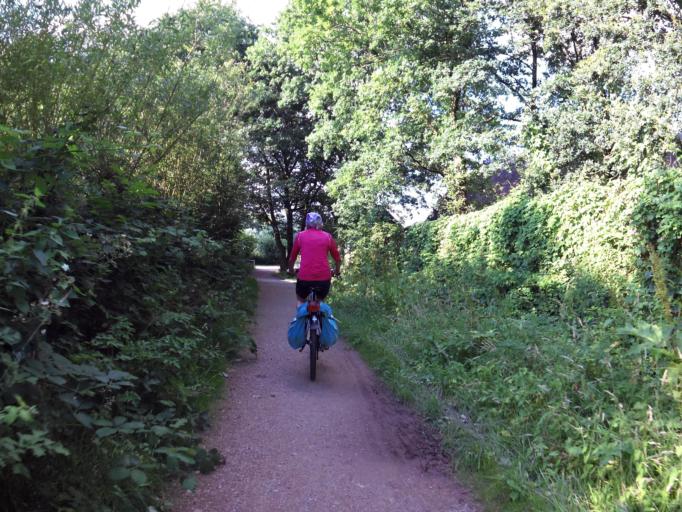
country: NL
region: North Brabant
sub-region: Gemeente Eindhoven
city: Eindhoven
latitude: 51.4224
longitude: 5.4758
